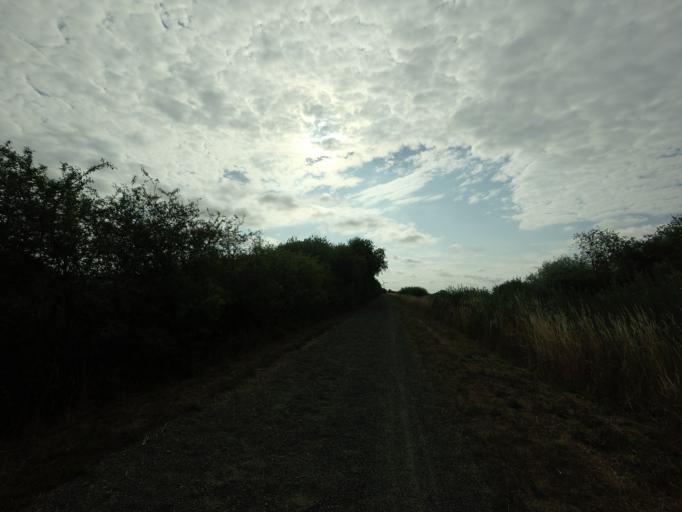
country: SE
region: Skane
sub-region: Helsingborg
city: Odakra
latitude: 56.1686
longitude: 12.7199
